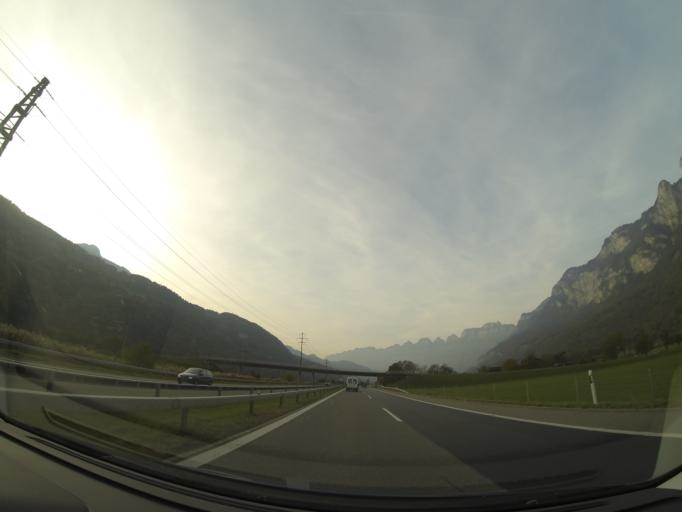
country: CH
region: Saint Gallen
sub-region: Wahlkreis Sarganserland
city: Sargans
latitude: 47.0641
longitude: 9.3904
